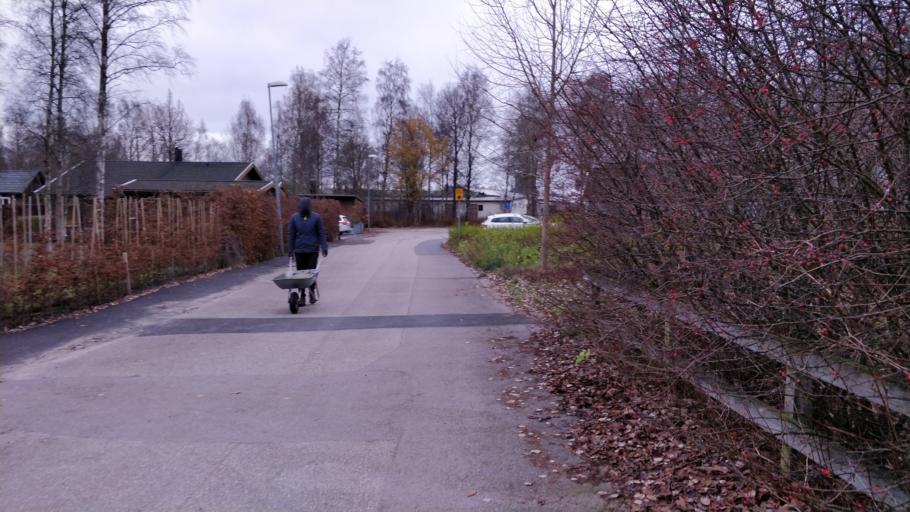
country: SE
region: Kronoberg
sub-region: Almhults Kommun
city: AElmhult
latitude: 56.5470
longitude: 14.1305
